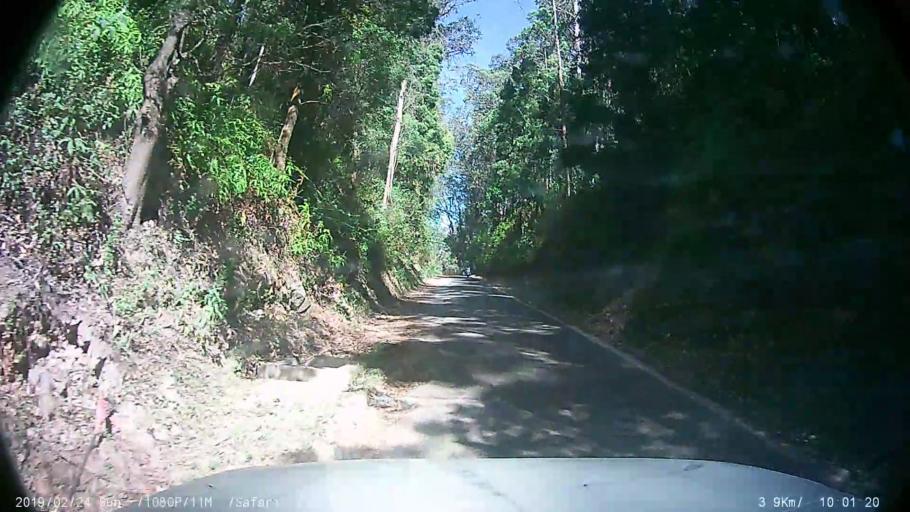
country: IN
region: Tamil Nadu
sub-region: Nilgiri
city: Aravankadu
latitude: 11.3647
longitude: 76.7576
